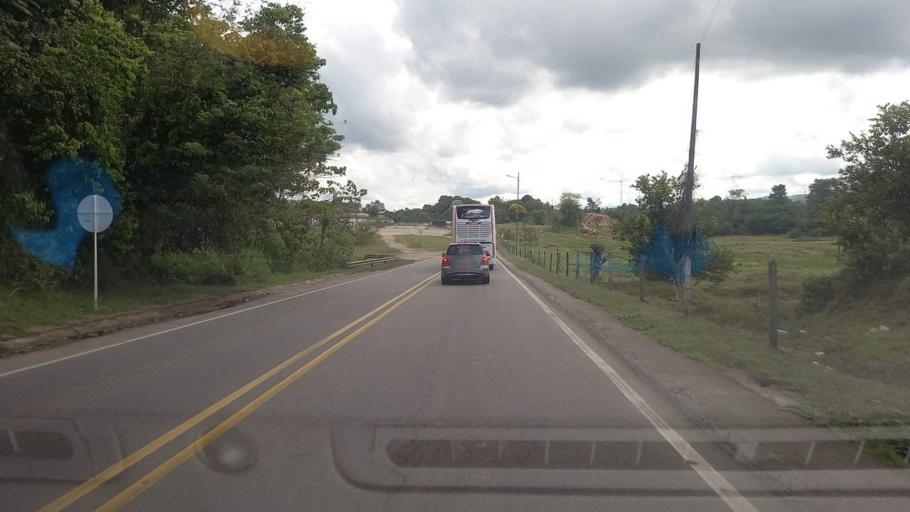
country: CO
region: Santander
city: Barrancabermeja
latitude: 7.1226
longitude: -73.5902
